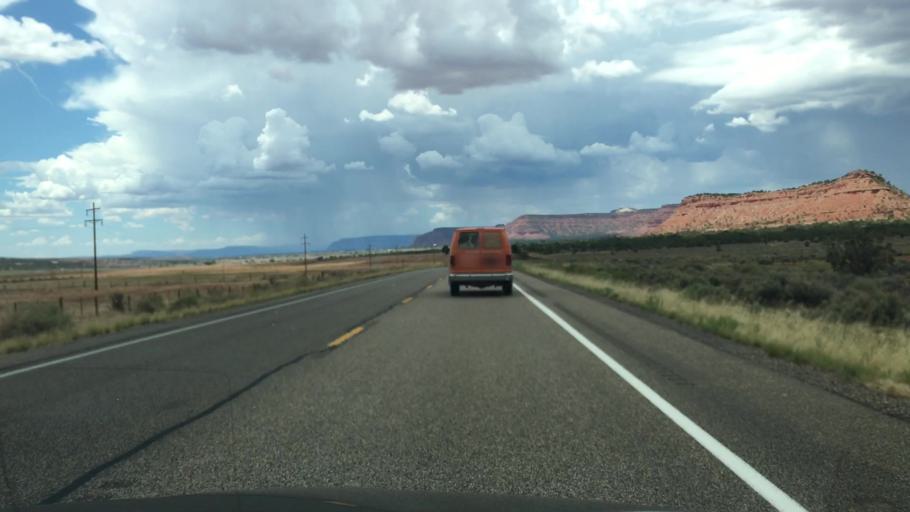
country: US
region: Utah
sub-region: Kane County
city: Kanab
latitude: 37.0386
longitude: -112.3206
